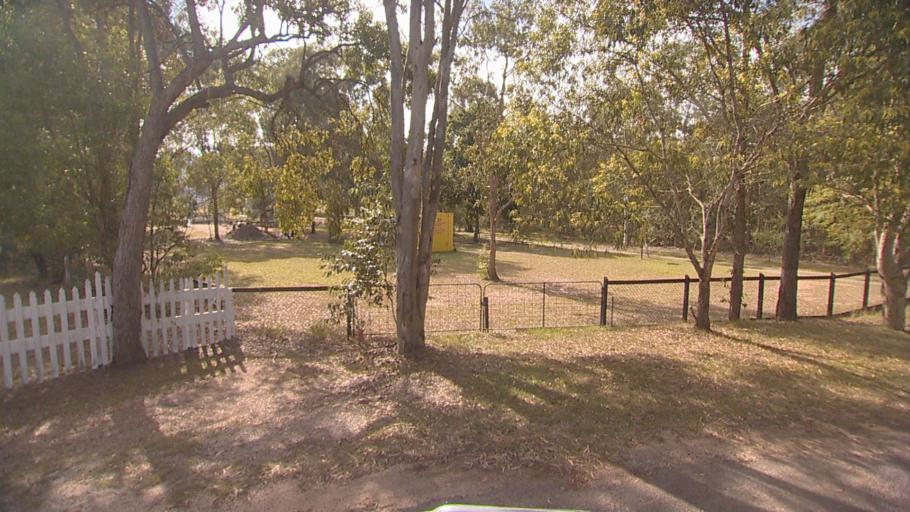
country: AU
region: Queensland
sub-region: Logan
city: North Maclean
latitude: -27.7335
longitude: 152.9814
